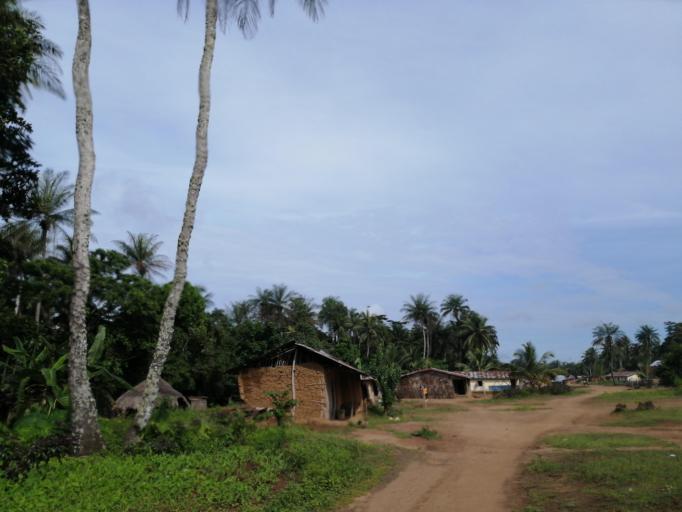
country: SL
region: Northern Province
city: Port Loko
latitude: 8.7904
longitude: -12.9322
